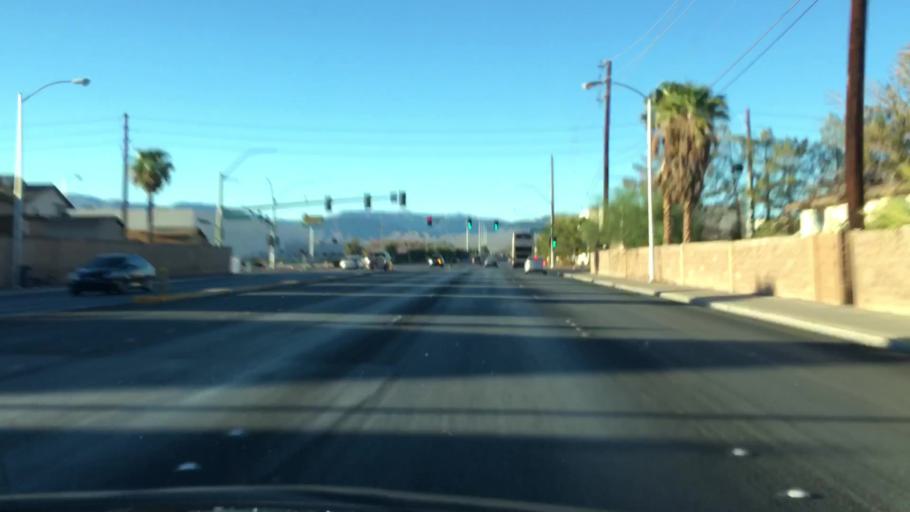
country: US
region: Nevada
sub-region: Clark County
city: Sunrise Manor
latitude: 36.2319
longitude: -115.0801
